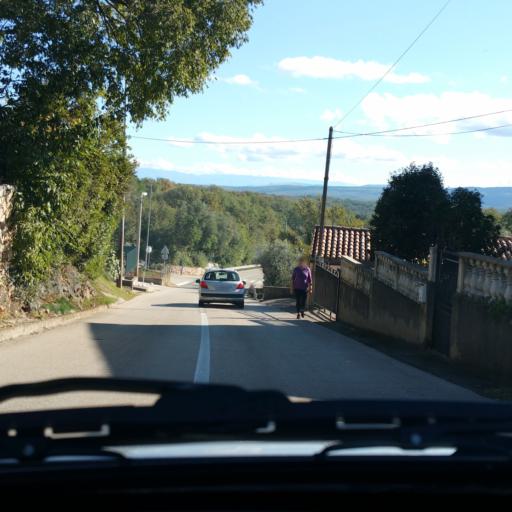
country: HR
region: Primorsko-Goranska
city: Omisalj
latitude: 45.2087
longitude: 14.5586
